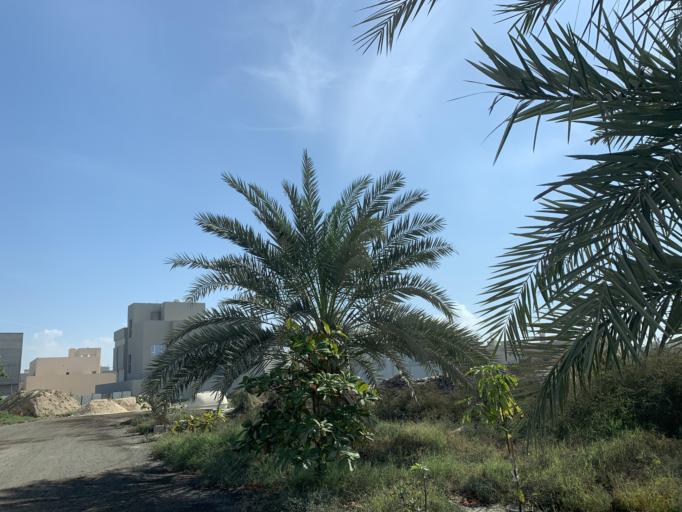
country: BH
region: Central Governorate
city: Madinat Hamad
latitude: 26.1262
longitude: 50.4730
